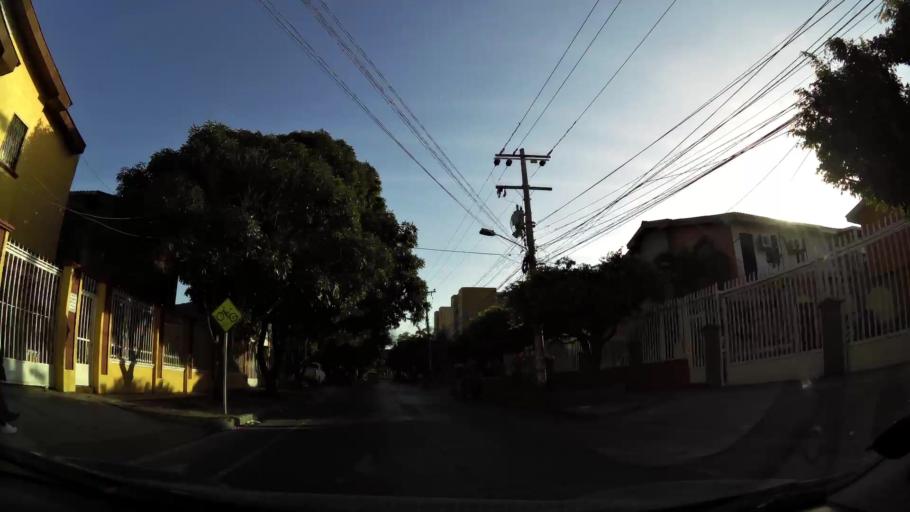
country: CO
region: Atlantico
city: Barranquilla
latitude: 10.9880
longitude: -74.7913
